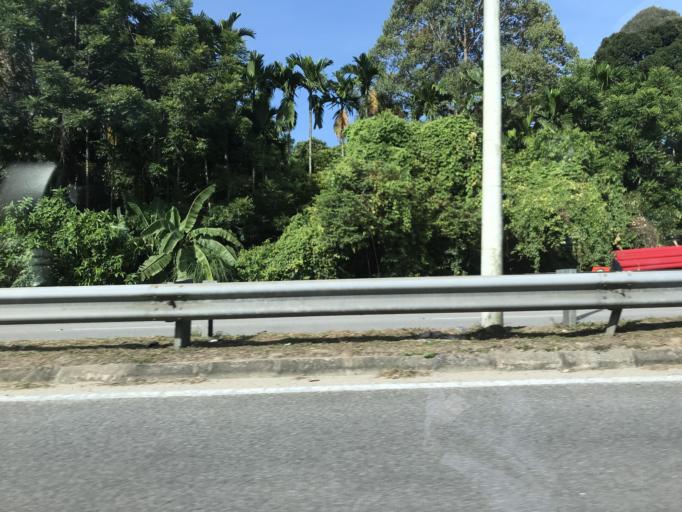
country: MY
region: Kelantan
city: Pasir Mas
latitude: 6.0613
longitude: 102.2084
